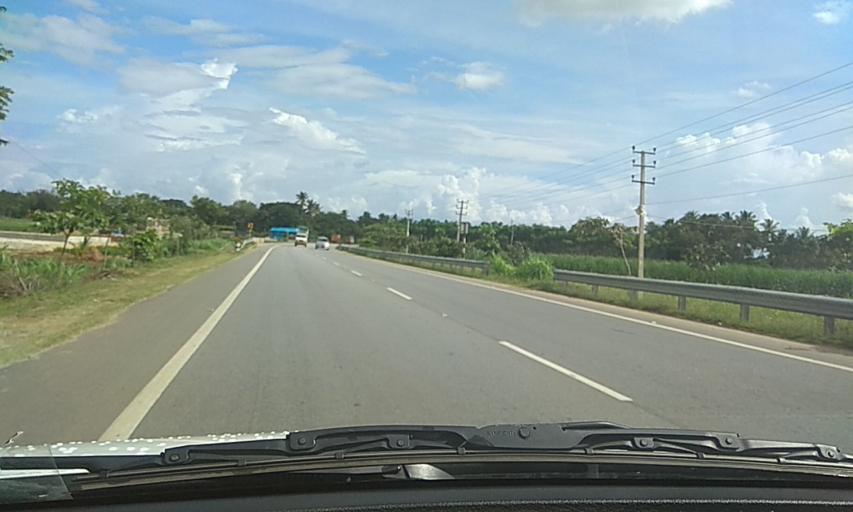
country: IN
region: Karnataka
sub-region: Mandya
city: Maddur
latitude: 12.6505
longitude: 77.0539
